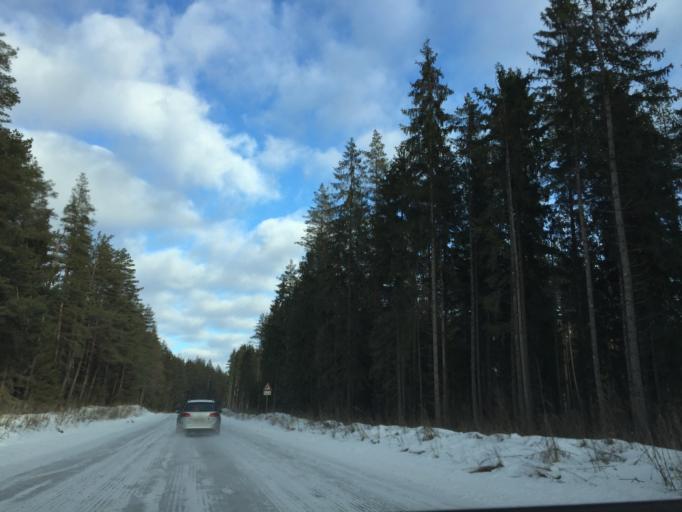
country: LV
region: Ogre
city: Jumprava
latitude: 56.5722
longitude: 24.9366
